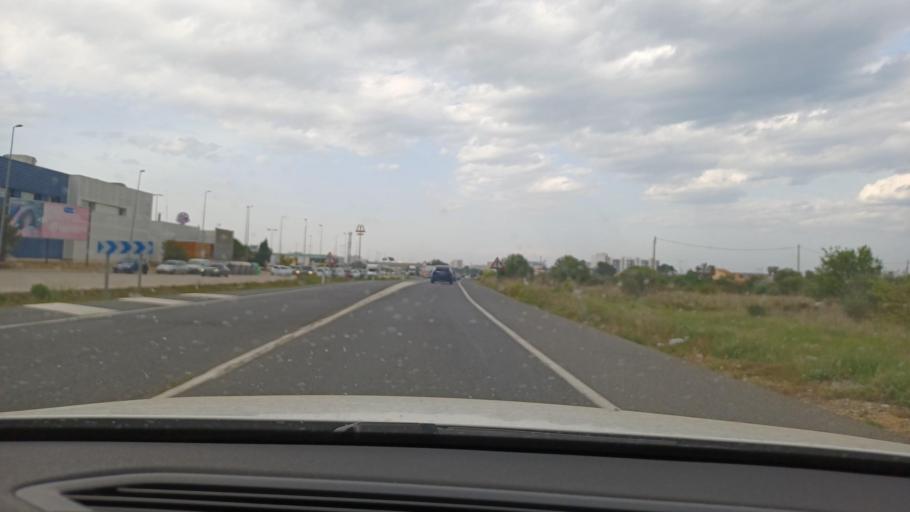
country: ES
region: Valencia
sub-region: Provincia de Castello
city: Vinaros
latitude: 40.4528
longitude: 0.4518
